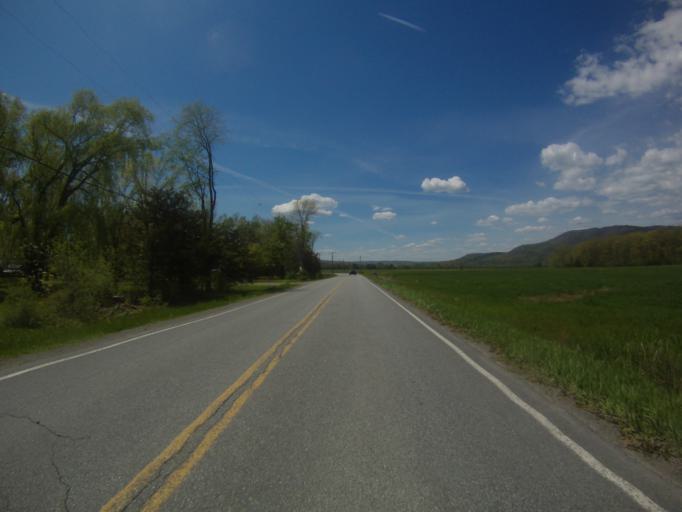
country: US
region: New York
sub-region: Essex County
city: Port Henry
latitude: 43.9953
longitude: -73.4205
